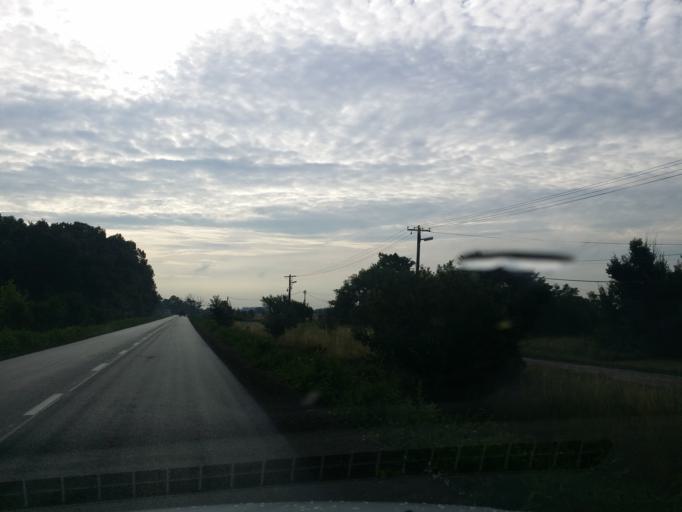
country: HU
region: Heves
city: Poroszlo
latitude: 47.6266
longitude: 20.6041
